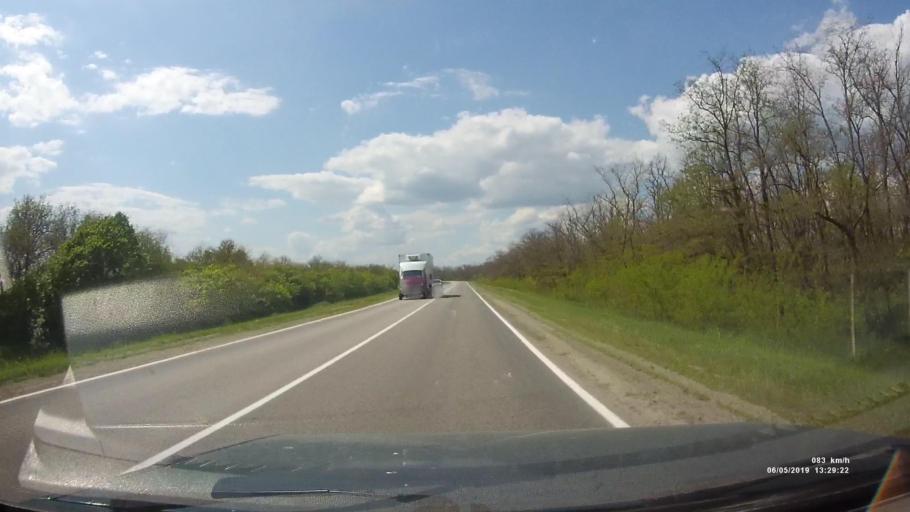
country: RU
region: Rostov
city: Ust'-Donetskiy
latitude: 47.6709
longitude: 40.8460
